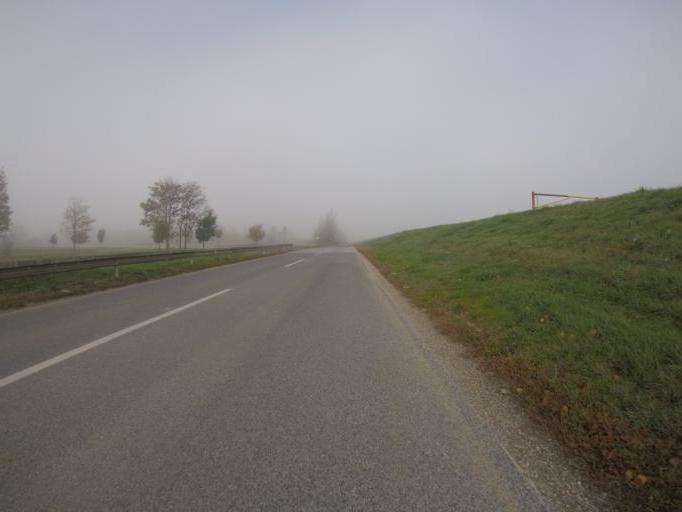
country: HR
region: Zagrebacka
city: Micevec
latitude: 45.7586
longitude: 16.0438
